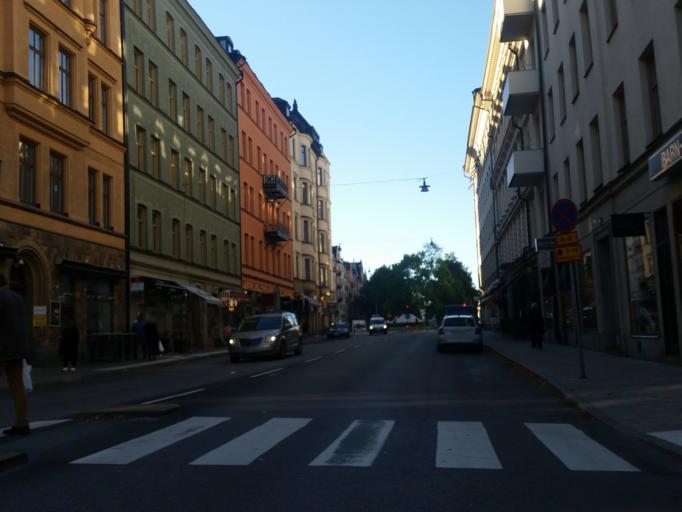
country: SE
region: Stockholm
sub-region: Stockholms Kommun
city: Stockholm
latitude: 59.3299
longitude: 18.0436
